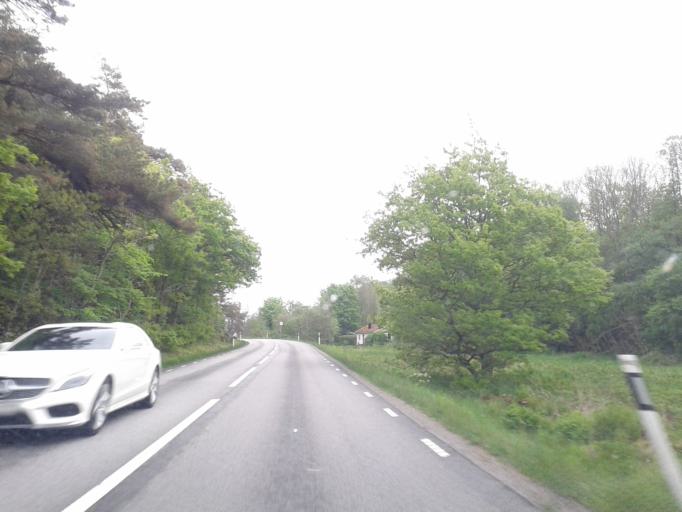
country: SE
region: Vaestra Goetaland
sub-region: Kungalvs Kommun
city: Kode
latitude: 57.8909
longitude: 11.7471
